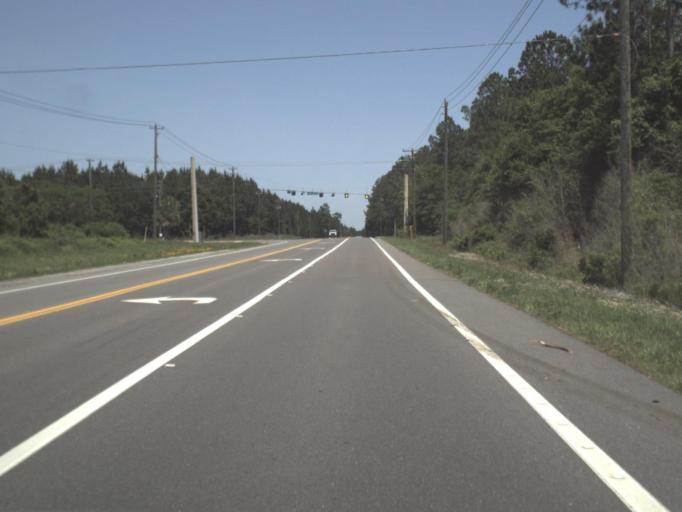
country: US
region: Florida
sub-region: Baker County
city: Macclenny
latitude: 30.2891
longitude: -82.0824
